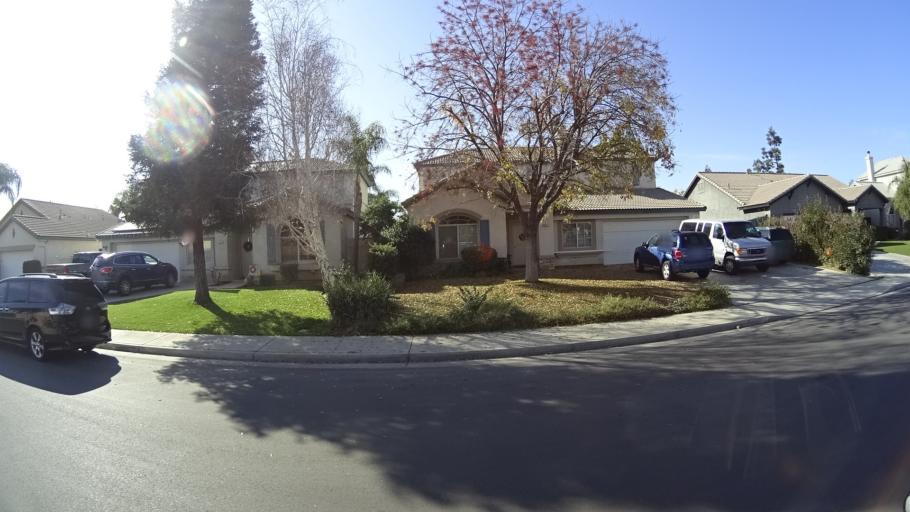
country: US
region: California
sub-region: Kern County
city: Greenacres
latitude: 35.4087
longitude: -119.1003
